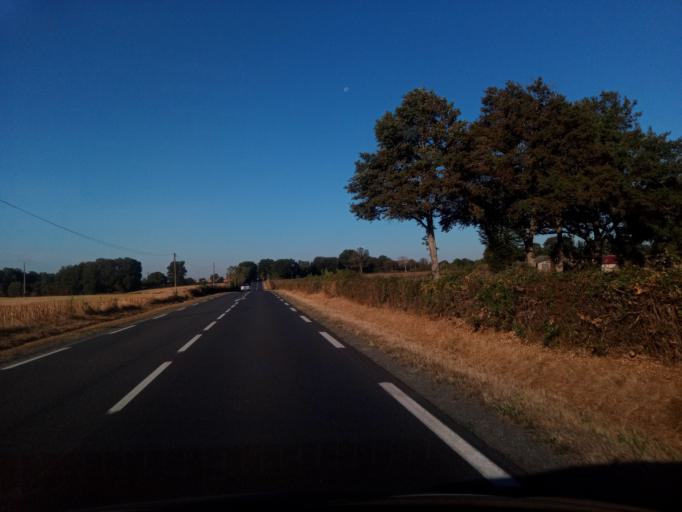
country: FR
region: Poitou-Charentes
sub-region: Departement de la Vienne
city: Montmorillon
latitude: 46.4089
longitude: 0.8039
